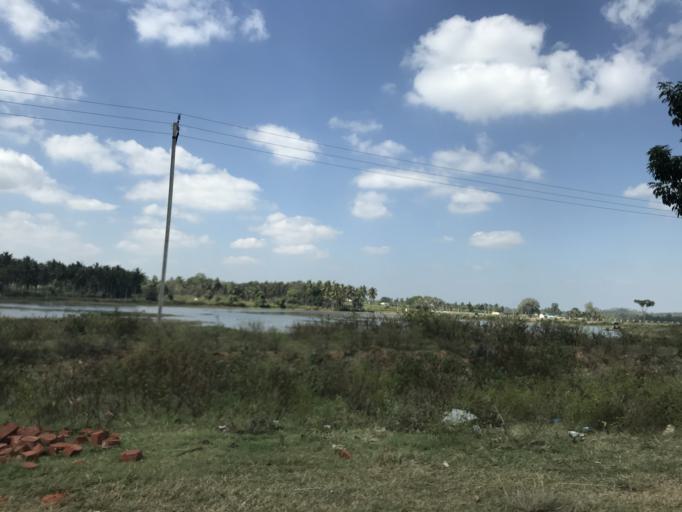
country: IN
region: Karnataka
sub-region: Mysore
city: Hunsur
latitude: 12.2927
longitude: 76.2899
